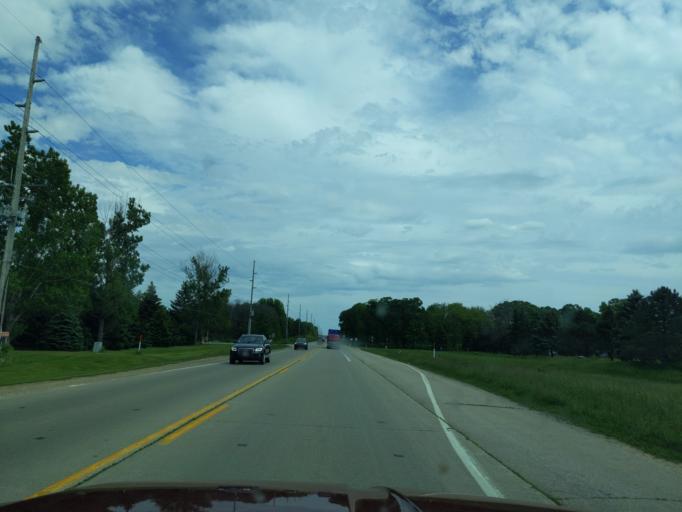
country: US
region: Wisconsin
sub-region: Dane County
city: Windsor
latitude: 43.1924
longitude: -89.2849
